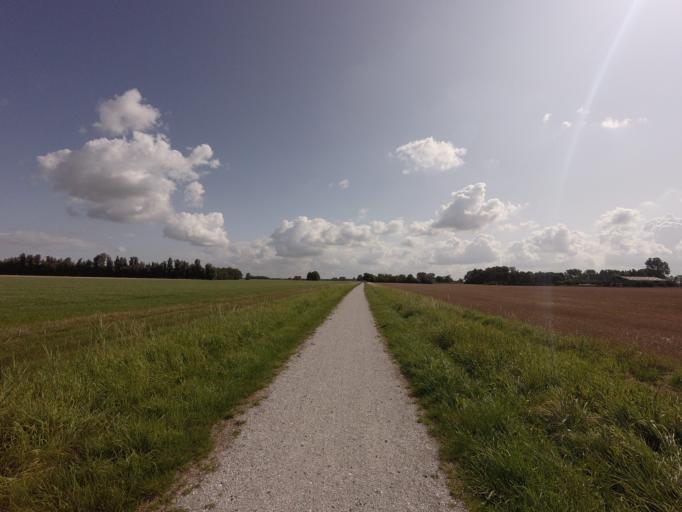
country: NL
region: Friesland
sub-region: Gemeente Het Bildt
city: Sint Annaparochie
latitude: 53.2800
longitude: 5.6697
